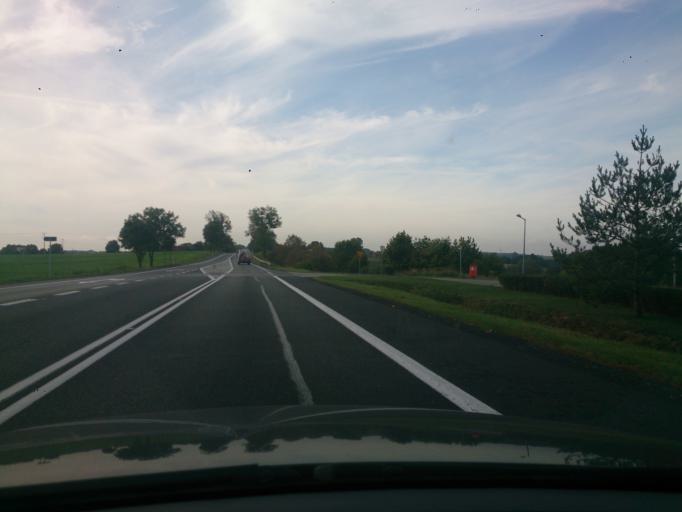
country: PL
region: Kujawsko-Pomorskie
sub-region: Powiat swiecki
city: Pruszcz
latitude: 53.3424
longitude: 18.2967
